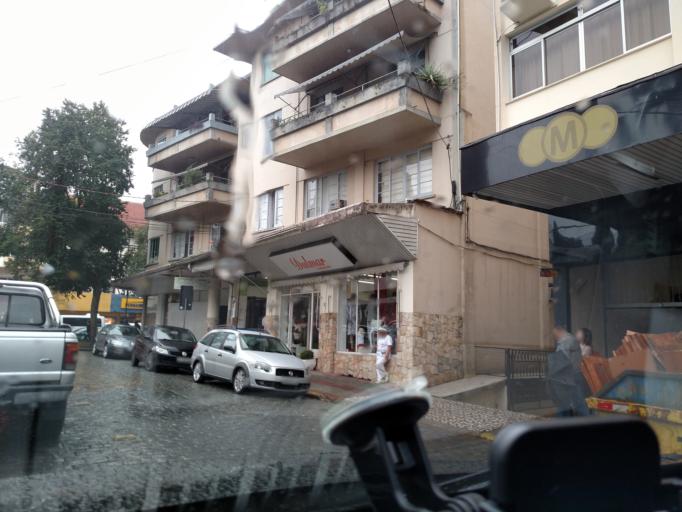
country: BR
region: Santa Catarina
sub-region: Blumenau
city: Blumenau
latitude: -26.9201
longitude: -49.0658
